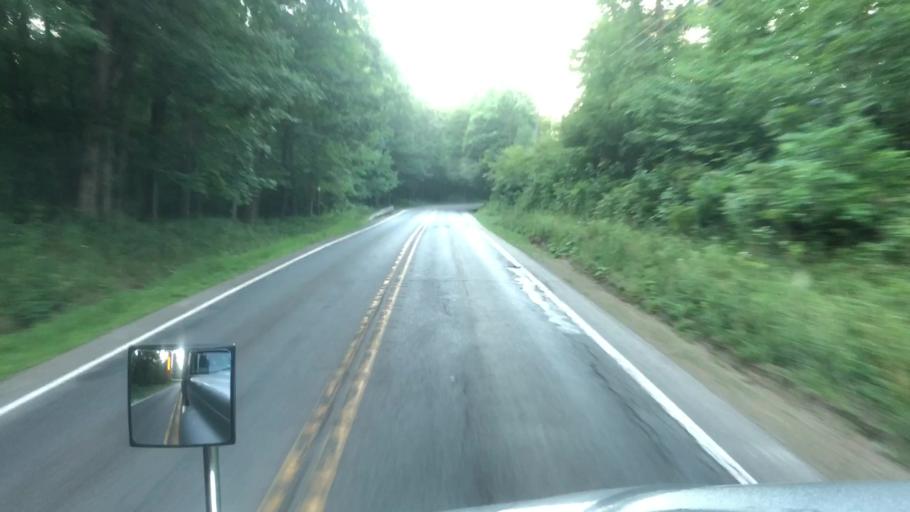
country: US
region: Pennsylvania
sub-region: Venango County
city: Hasson Heights
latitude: 41.5077
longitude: -79.6272
